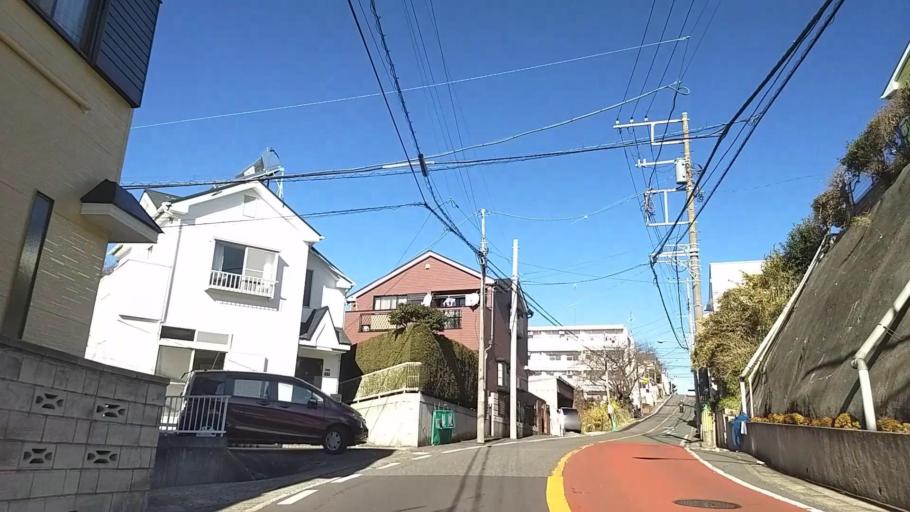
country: JP
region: Kanagawa
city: Yokohama
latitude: 35.4489
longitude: 139.5890
